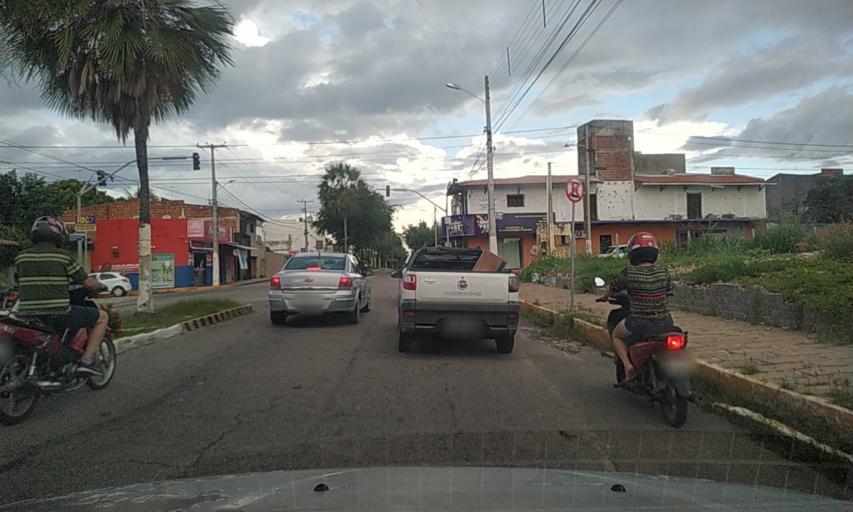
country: BR
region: Rio Grande do Norte
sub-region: Mossoro
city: Mossoro
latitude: -5.1877
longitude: -37.3513
